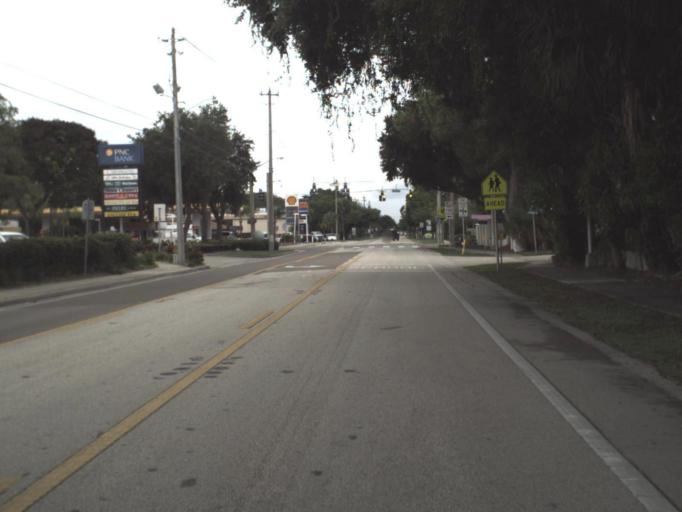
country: US
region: Florida
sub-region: Sarasota County
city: South Sarasota
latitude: 27.3018
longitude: -82.5336
